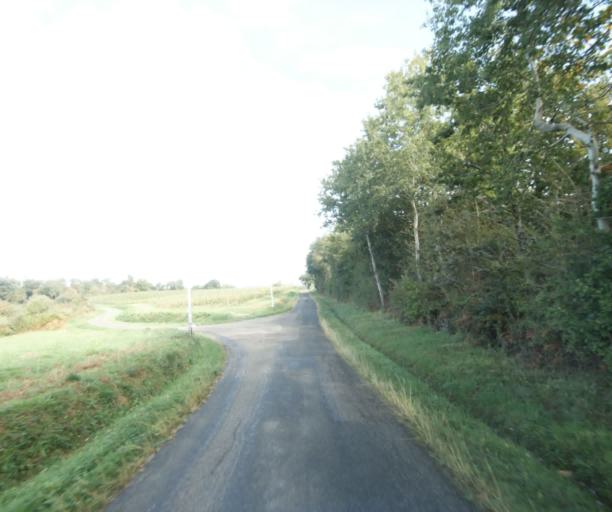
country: FR
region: Midi-Pyrenees
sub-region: Departement du Gers
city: Cazaubon
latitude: 43.8490
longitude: -0.0780
